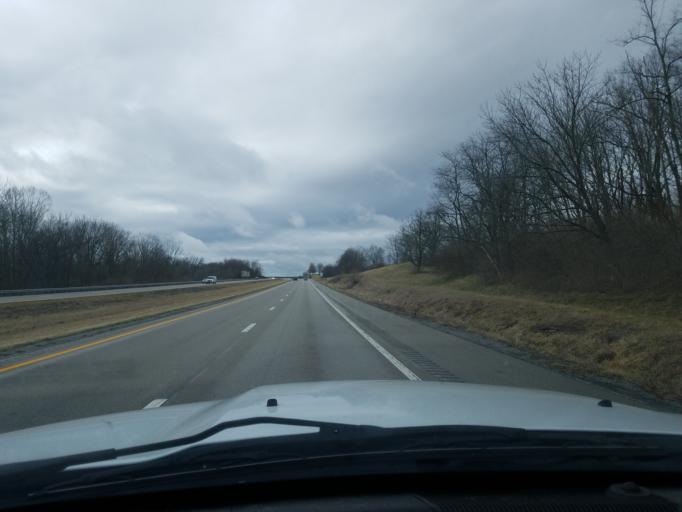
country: US
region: Kentucky
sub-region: Montgomery County
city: Mount Sterling
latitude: 38.0863
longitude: -83.9168
